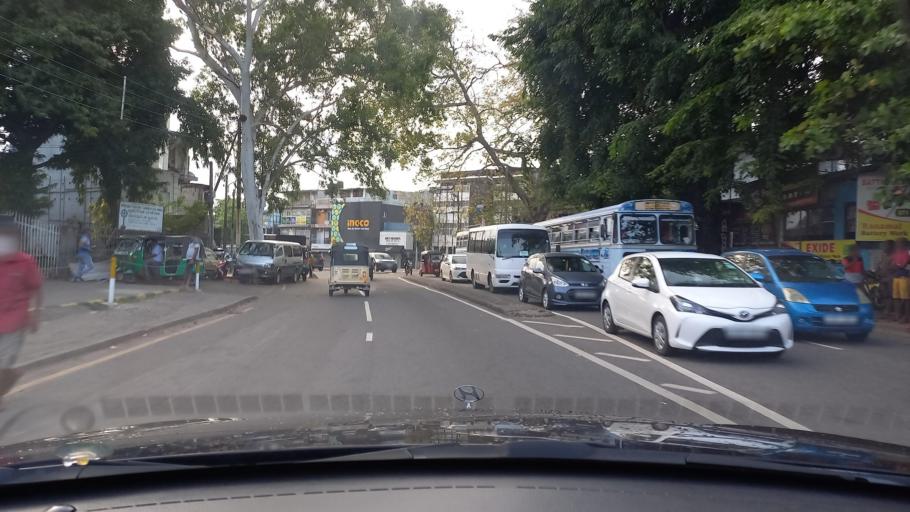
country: LK
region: Western
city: Pita Kotte
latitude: 6.8785
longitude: 79.8716
